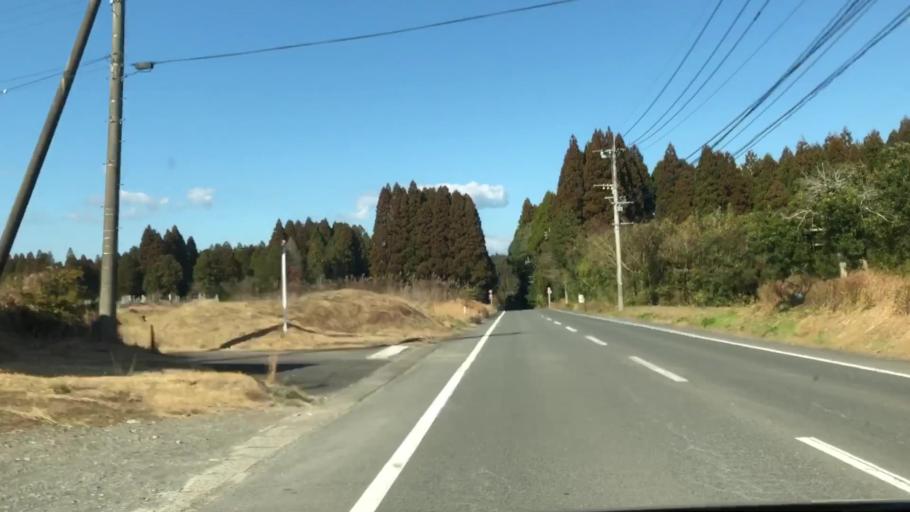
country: JP
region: Kagoshima
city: Satsumasendai
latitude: 31.8393
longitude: 130.4299
